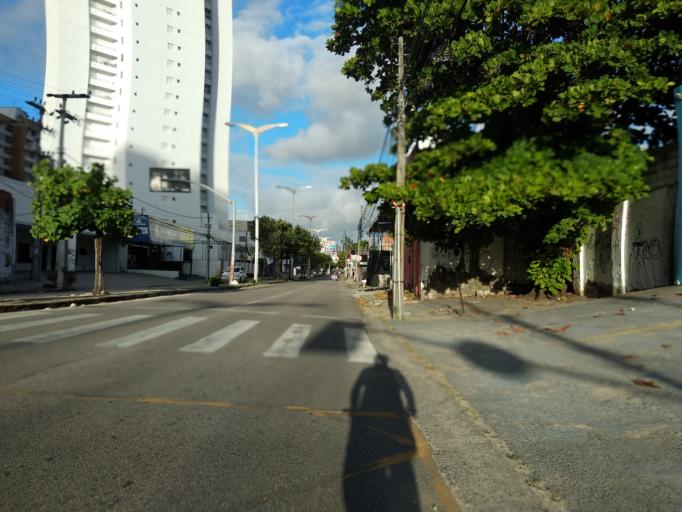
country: BR
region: Ceara
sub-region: Fortaleza
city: Fortaleza
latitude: -3.7360
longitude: -38.5167
